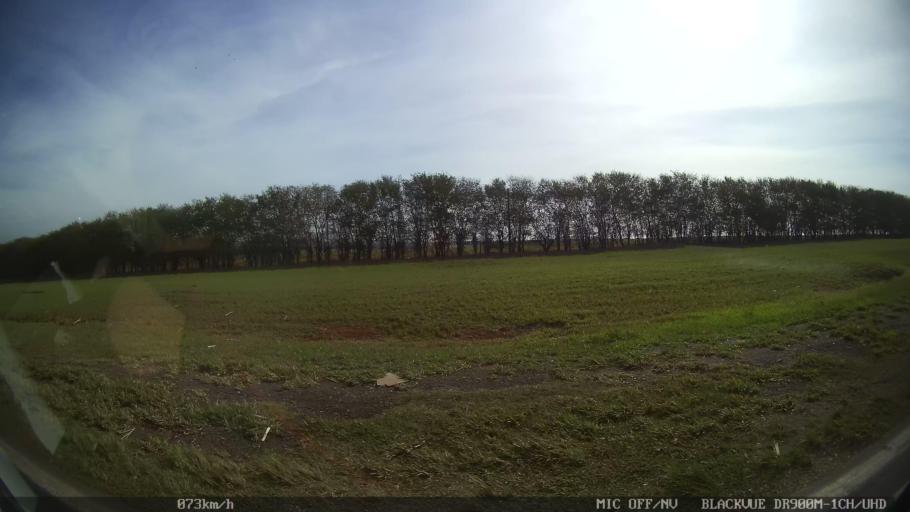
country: BR
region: Sao Paulo
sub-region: Rio Das Pedras
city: Rio das Pedras
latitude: -22.7966
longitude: -47.6038
